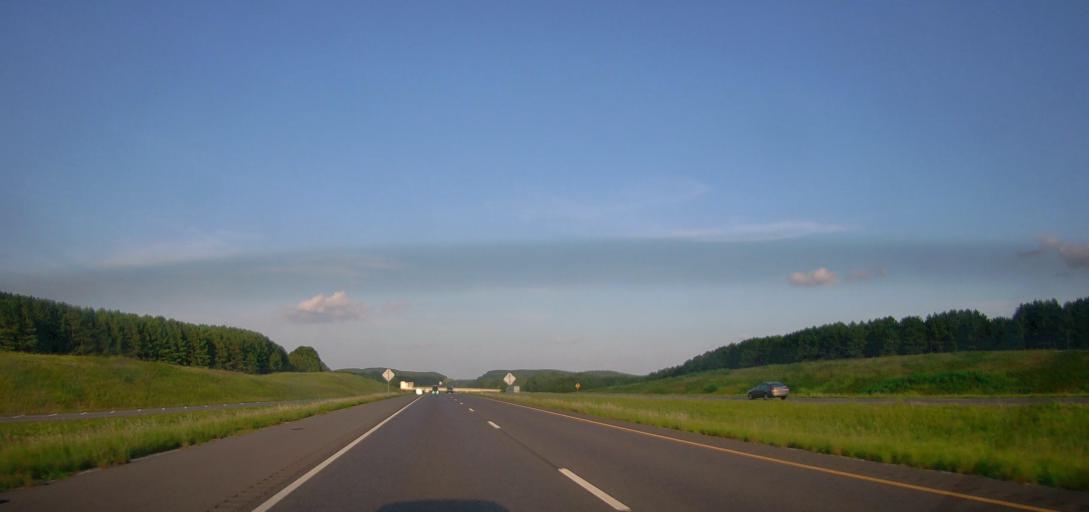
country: US
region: Alabama
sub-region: Walker County
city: Carbon Hill
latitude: 33.9516
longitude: -87.6140
